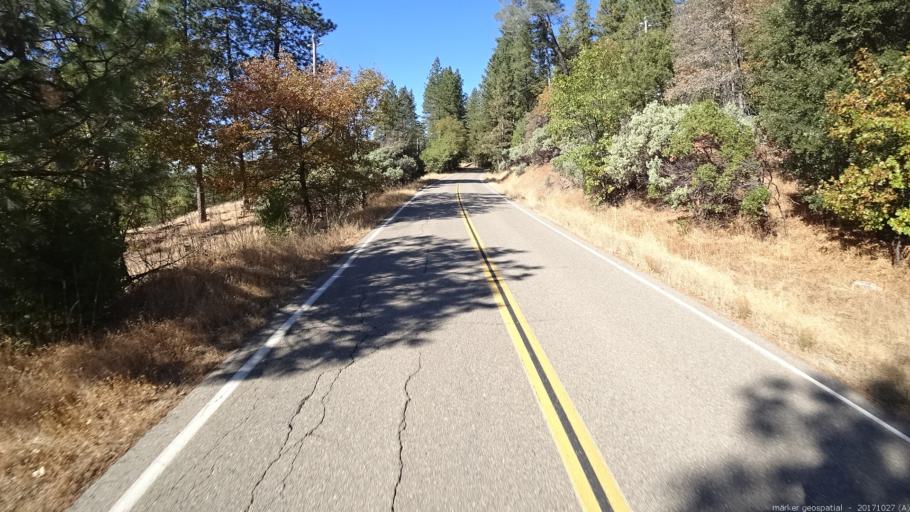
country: US
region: California
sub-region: Shasta County
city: Shingletown
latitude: 40.7067
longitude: -121.9309
